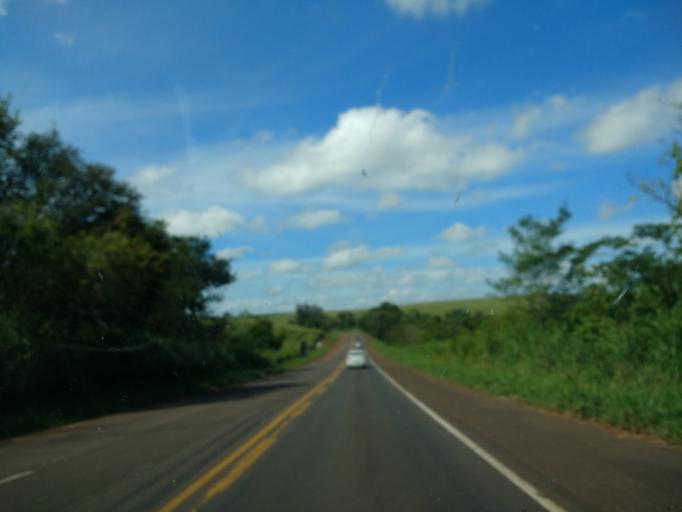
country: BR
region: Parana
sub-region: Cianorte
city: Cianorte
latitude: -23.6554
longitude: -52.5141
